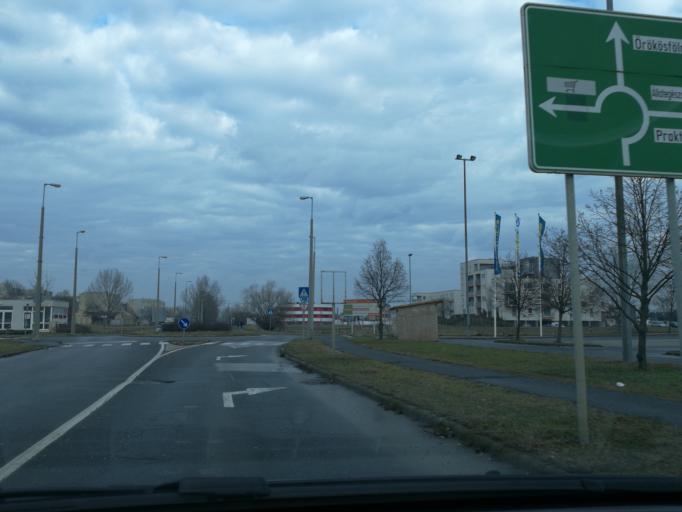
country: HU
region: Szabolcs-Szatmar-Bereg
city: Nyiregyhaza
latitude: 47.9531
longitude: 21.7438
